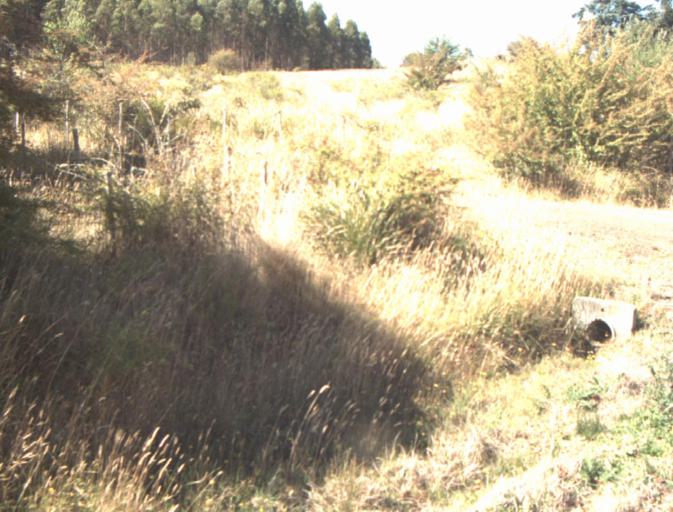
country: AU
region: Tasmania
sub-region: Launceston
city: Newstead
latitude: -41.3492
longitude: 147.3041
